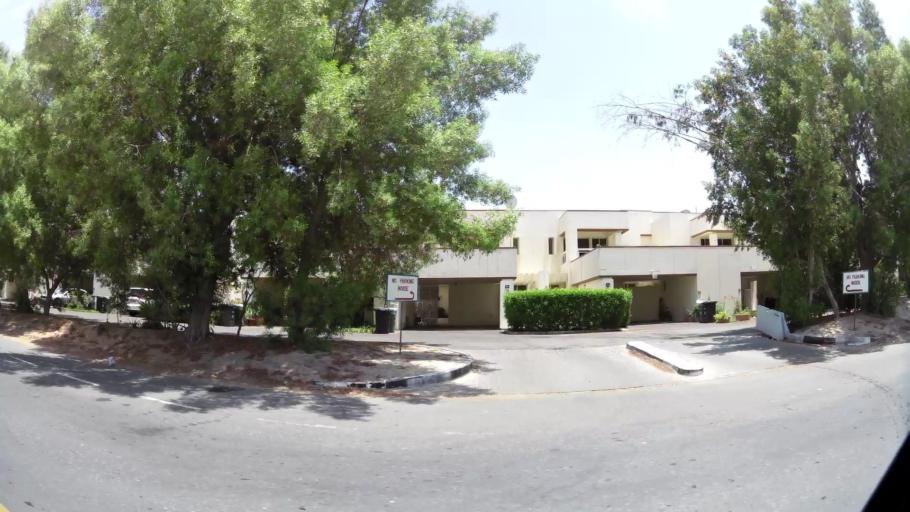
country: AE
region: Dubai
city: Dubai
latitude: 25.1782
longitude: 55.2427
